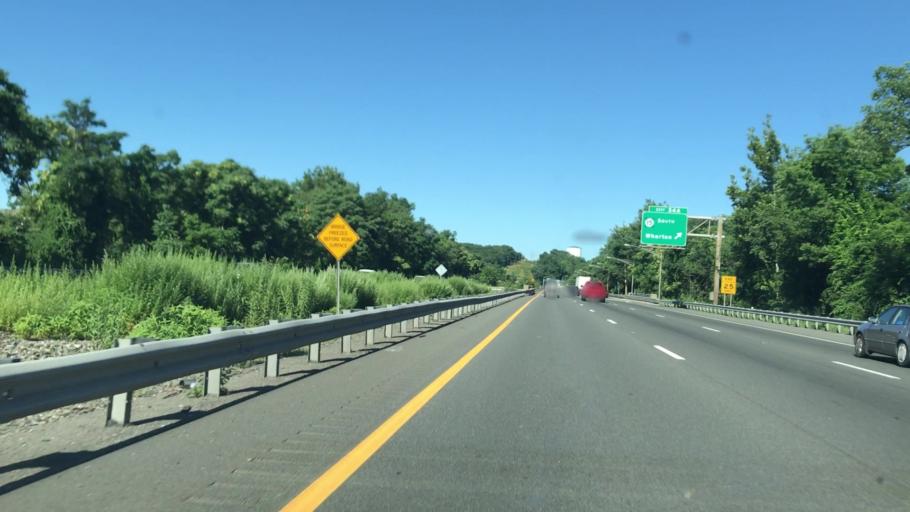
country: US
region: New Jersey
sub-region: Morris County
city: Wharton
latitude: 40.9096
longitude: -74.5704
